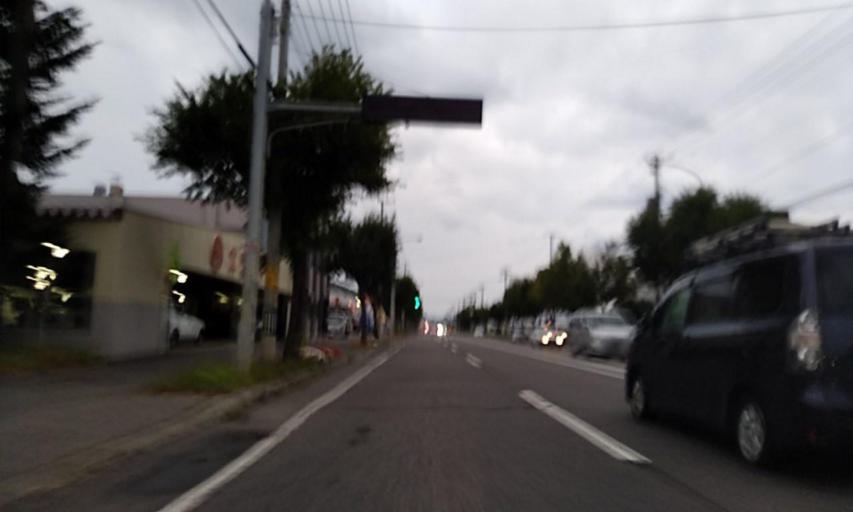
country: JP
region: Hokkaido
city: Abashiri
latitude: 44.0175
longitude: 144.2437
